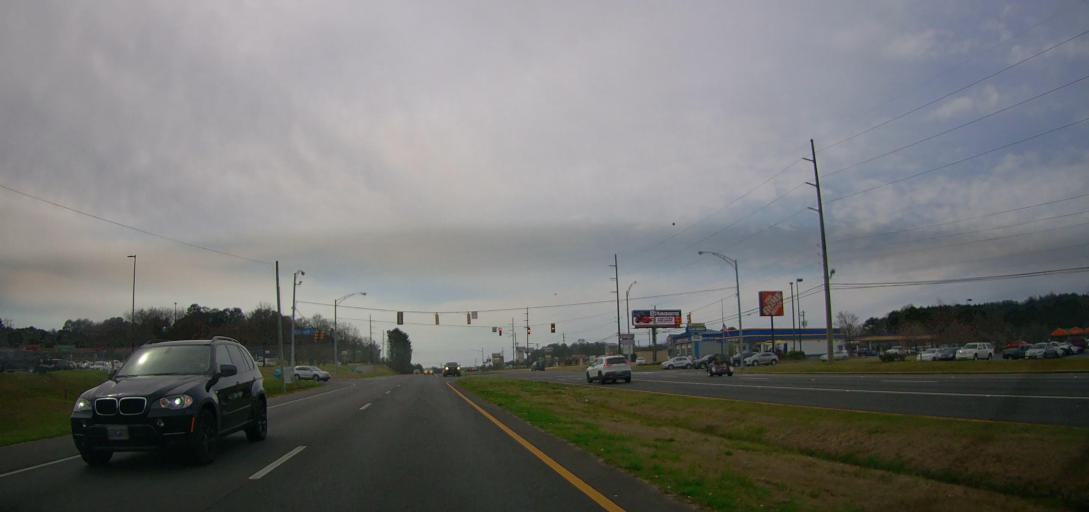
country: US
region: Alabama
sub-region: Walker County
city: Jasper
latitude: 33.8448
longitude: -87.2534
